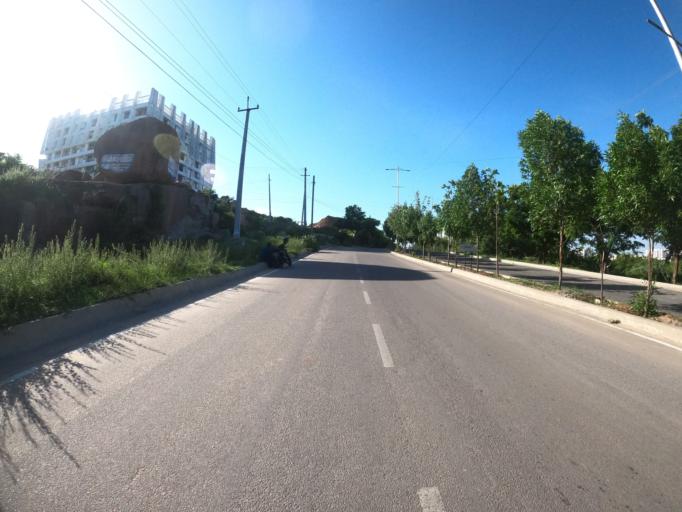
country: IN
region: Telangana
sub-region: Hyderabad
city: Hyderabad
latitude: 17.3535
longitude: 78.3697
